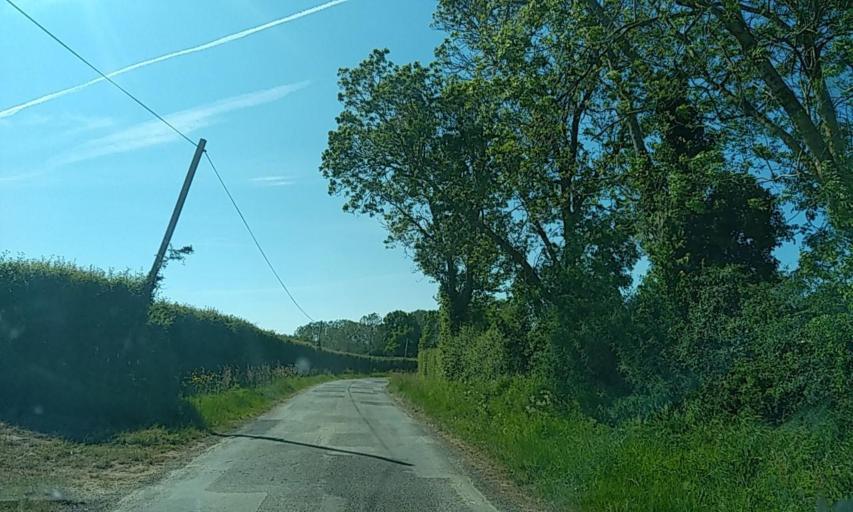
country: FR
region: Poitou-Charentes
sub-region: Departement des Deux-Sevres
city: Boisme
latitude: 46.7713
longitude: -0.4104
